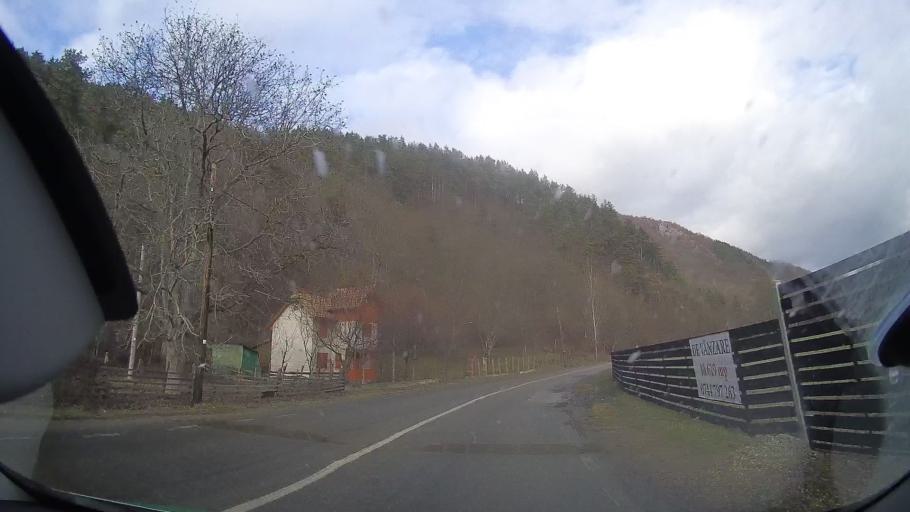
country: RO
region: Alba
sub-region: Comuna Ocolis
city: Ocolis
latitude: 46.4798
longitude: 23.5077
